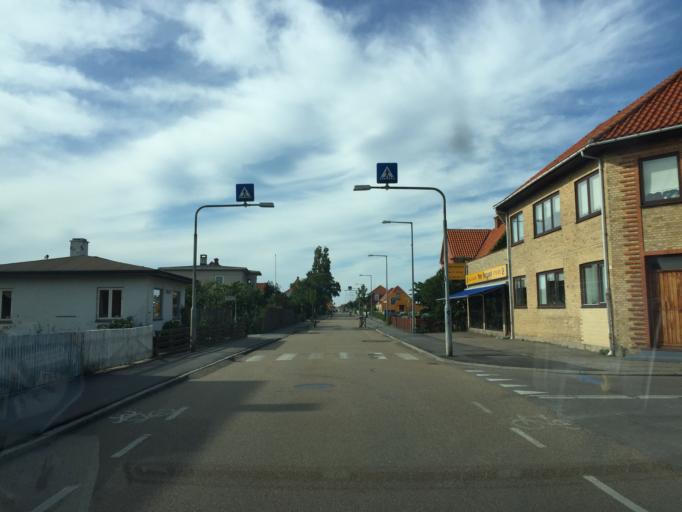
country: DK
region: Capital Region
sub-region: Halsnaes Kommune
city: Hundested
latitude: 55.9558
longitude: 11.8543
